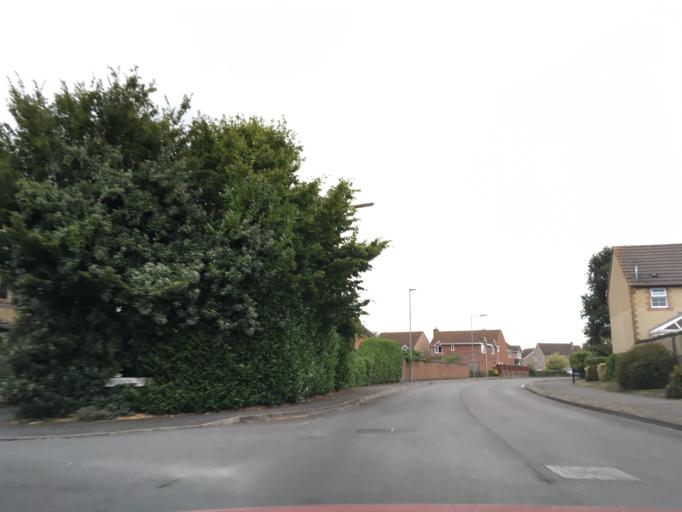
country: GB
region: England
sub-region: Wiltshire
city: Chippenham
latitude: 51.4467
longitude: -2.1095
